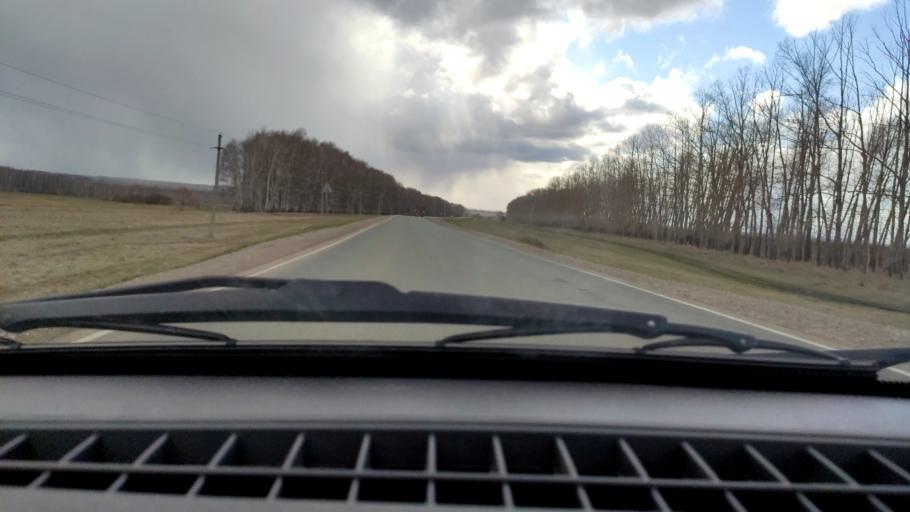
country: RU
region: Bashkortostan
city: Kushnarenkovo
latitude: 55.0576
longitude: 55.1596
